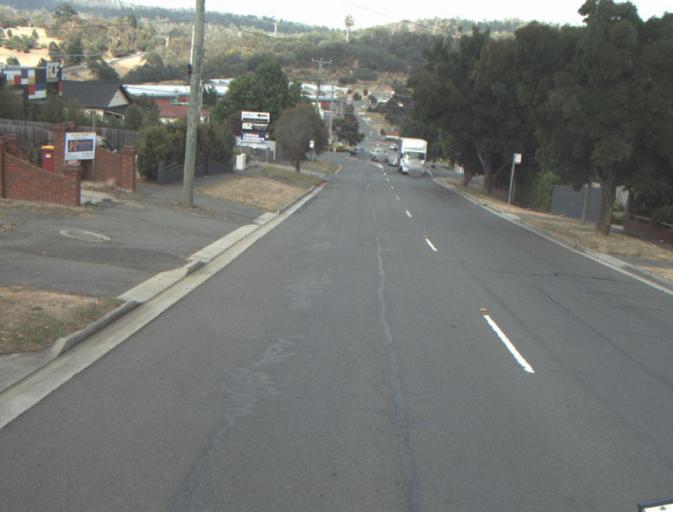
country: AU
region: Tasmania
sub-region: Launceston
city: East Launceston
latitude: -41.4739
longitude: 147.1670
